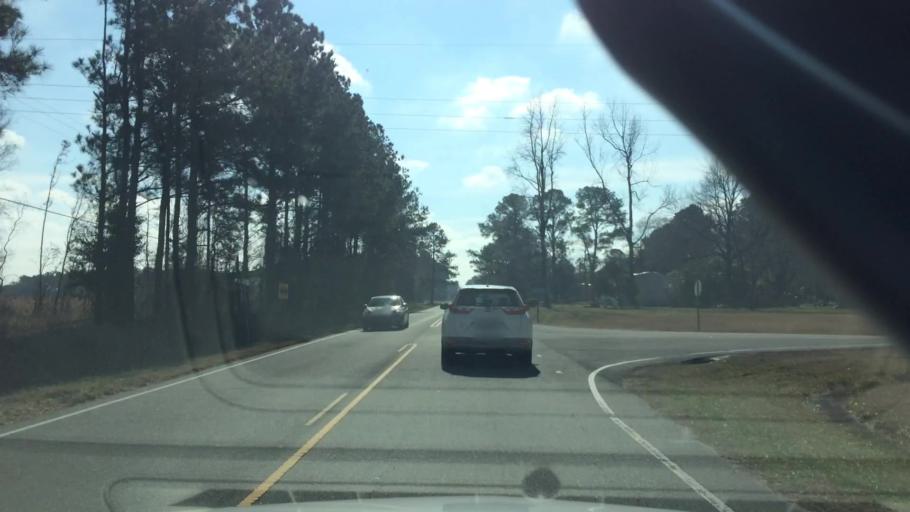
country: US
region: North Carolina
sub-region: Duplin County
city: Beulaville
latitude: 34.8757
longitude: -77.7905
